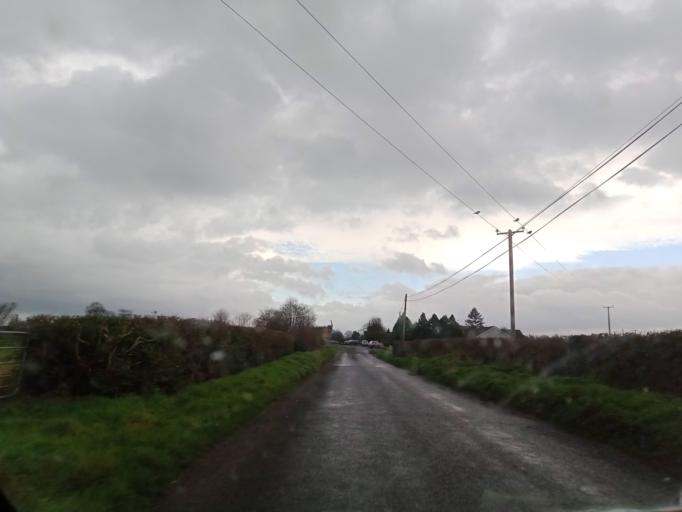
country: IE
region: Munster
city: Thurles
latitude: 52.6319
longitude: -7.7823
